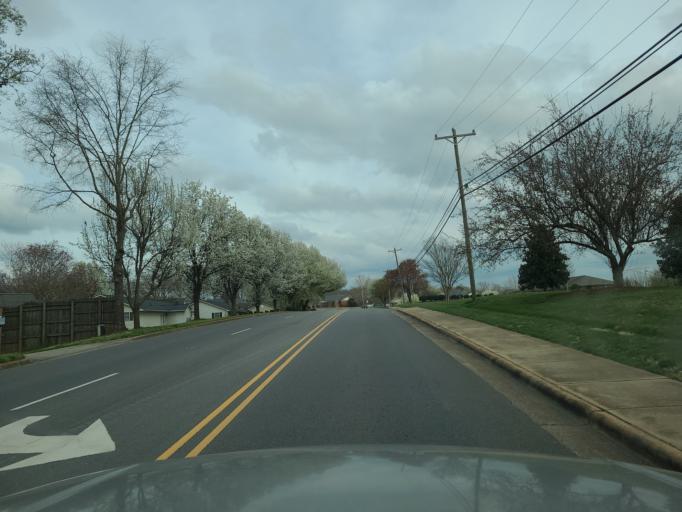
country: US
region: North Carolina
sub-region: Cleveland County
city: Boiling Springs
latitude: 35.2512
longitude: -81.6768
